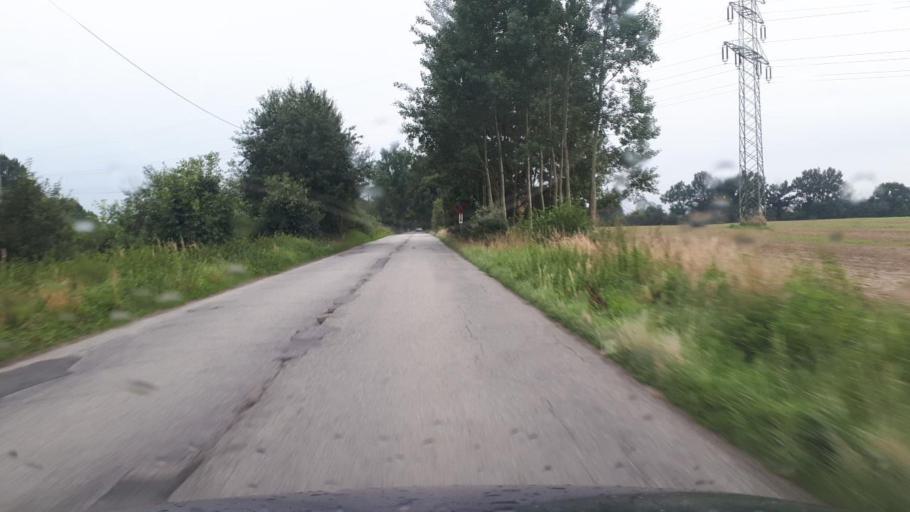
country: PL
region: Silesian Voivodeship
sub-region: Powiat tarnogorski
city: Wieszowa
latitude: 50.3769
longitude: 18.7157
